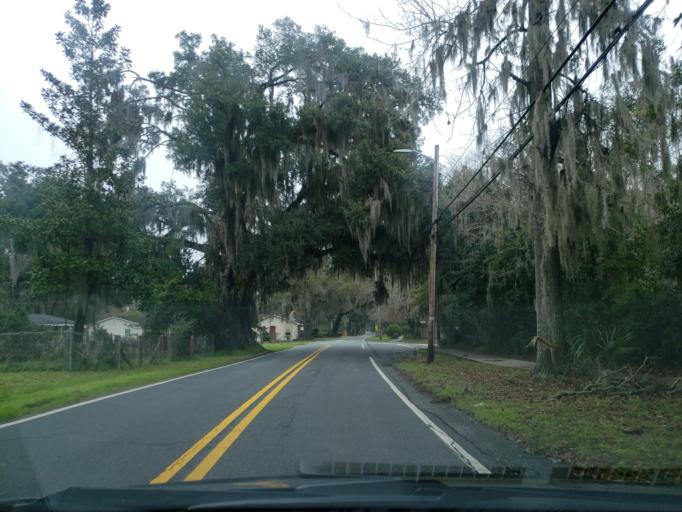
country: US
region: Georgia
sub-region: Chatham County
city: Montgomery
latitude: 31.9445
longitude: -81.1484
